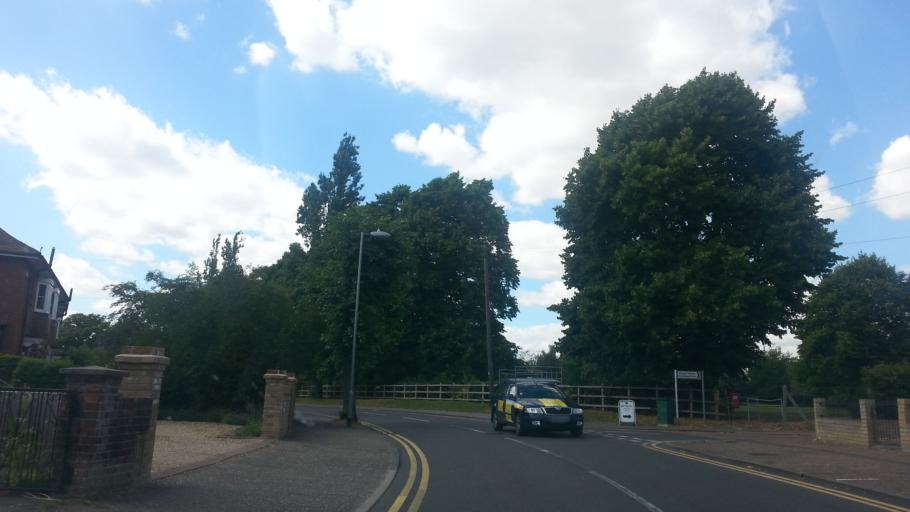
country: GB
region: England
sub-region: Essex
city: Chelmsford
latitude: 51.7366
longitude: 0.4889
